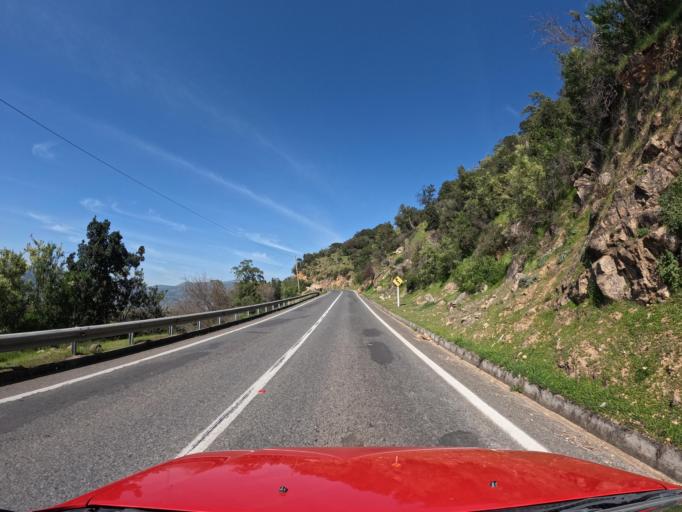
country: CL
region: Maule
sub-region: Provincia de Curico
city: Rauco
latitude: -35.0468
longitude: -71.5937
